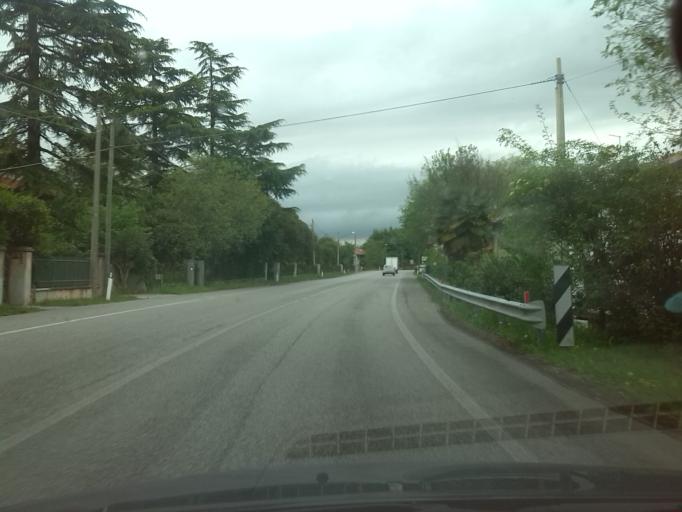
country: IT
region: Friuli Venezia Giulia
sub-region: Provincia di Gorizia
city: Gradisca d'Isonzo
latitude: 45.8970
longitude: 13.5054
